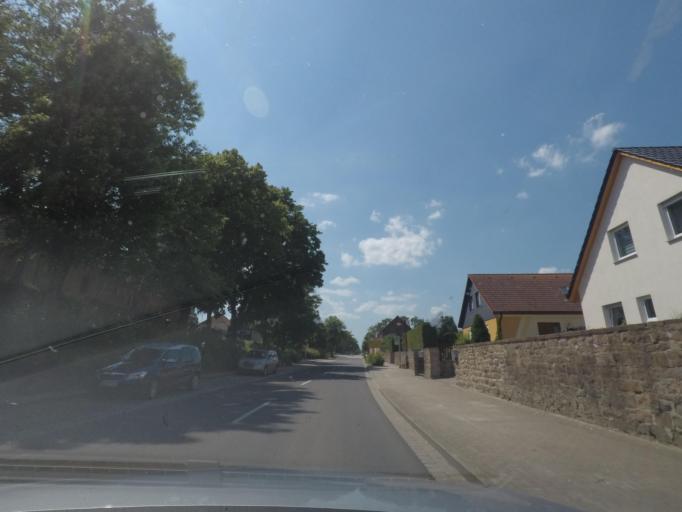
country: DE
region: Saxony-Anhalt
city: Eichenbarleben
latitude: 52.2117
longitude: 11.3982
